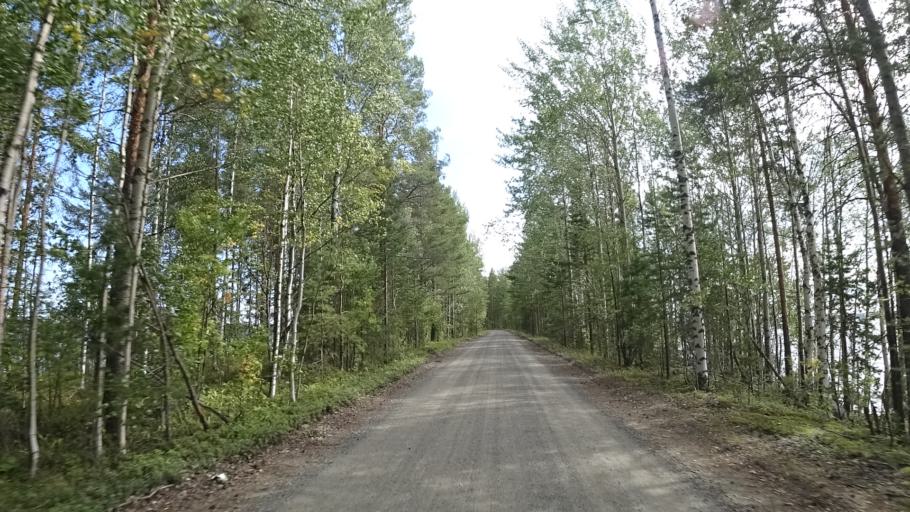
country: FI
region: North Karelia
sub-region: Keski-Karjala
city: Raeaekkylae
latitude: 62.3895
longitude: 29.7829
